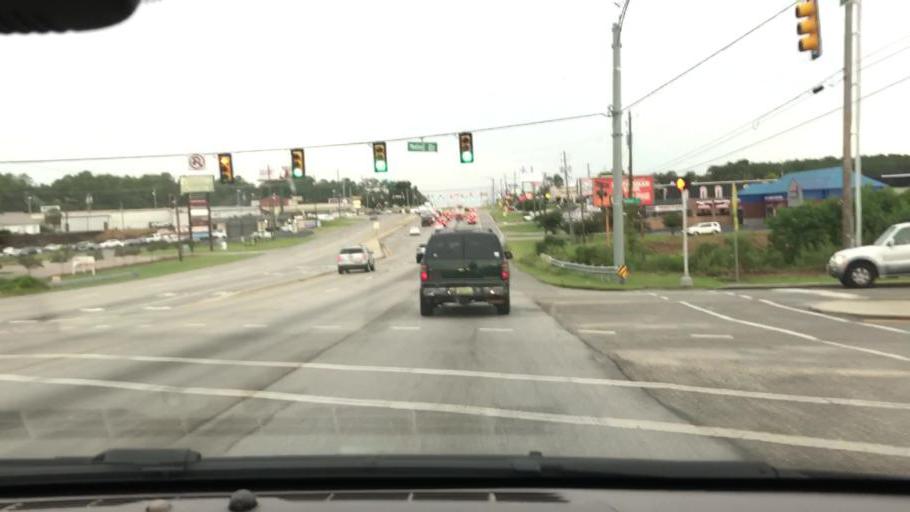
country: US
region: Alabama
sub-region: Houston County
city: Dothan
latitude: 31.2552
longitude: -85.4310
